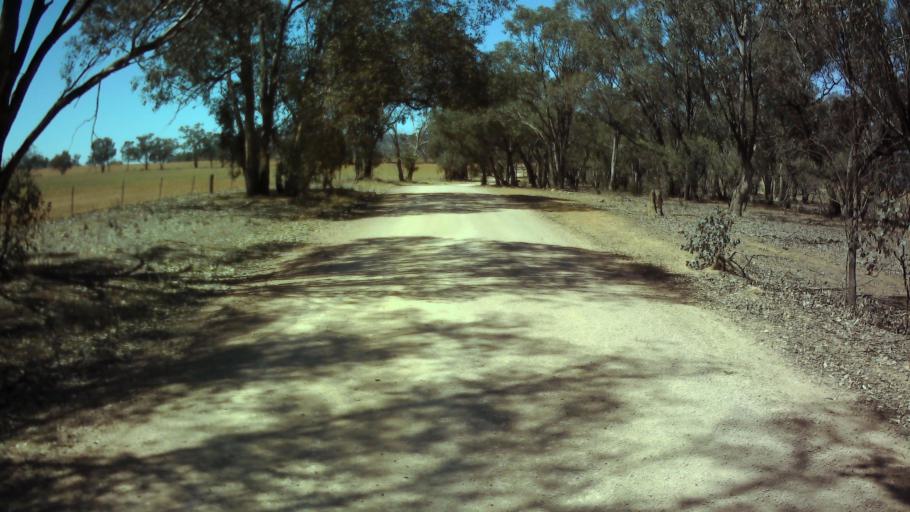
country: AU
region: New South Wales
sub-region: Weddin
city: Grenfell
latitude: -33.9279
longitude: 148.0781
